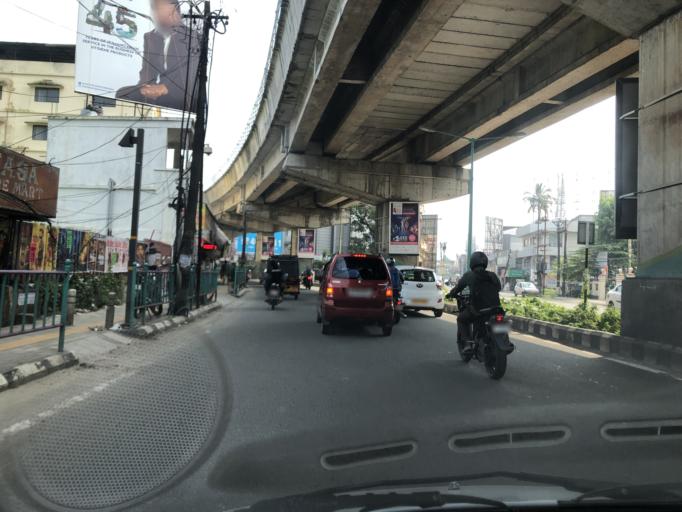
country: IN
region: Kerala
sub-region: Ernakulam
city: Elur
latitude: 10.0017
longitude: 76.3028
